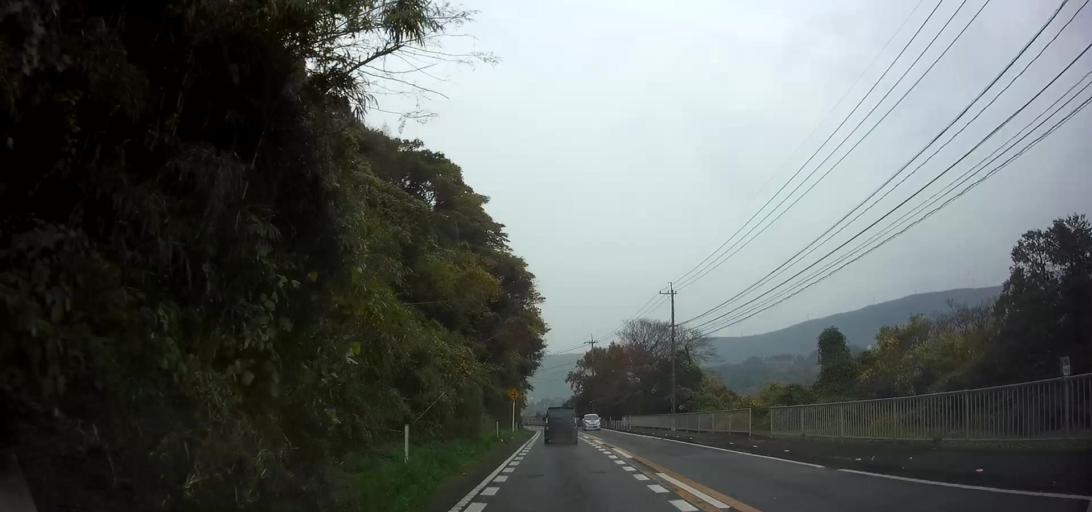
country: JP
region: Nagasaki
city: Shimabara
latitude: 32.7784
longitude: 130.2100
